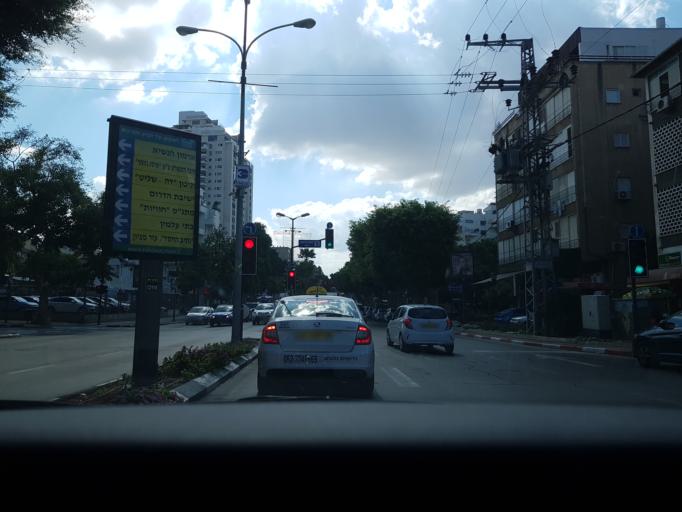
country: IL
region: Central District
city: Ness Ziona
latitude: 31.9030
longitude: 34.8082
